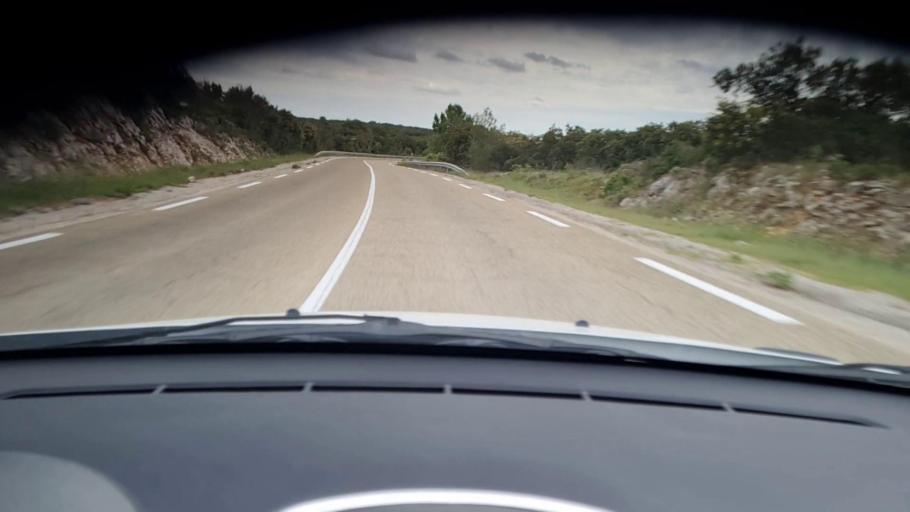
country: FR
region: Languedoc-Roussillon
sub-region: Departement du Gard
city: Poulx
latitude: 43.9037
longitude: 4.3940
